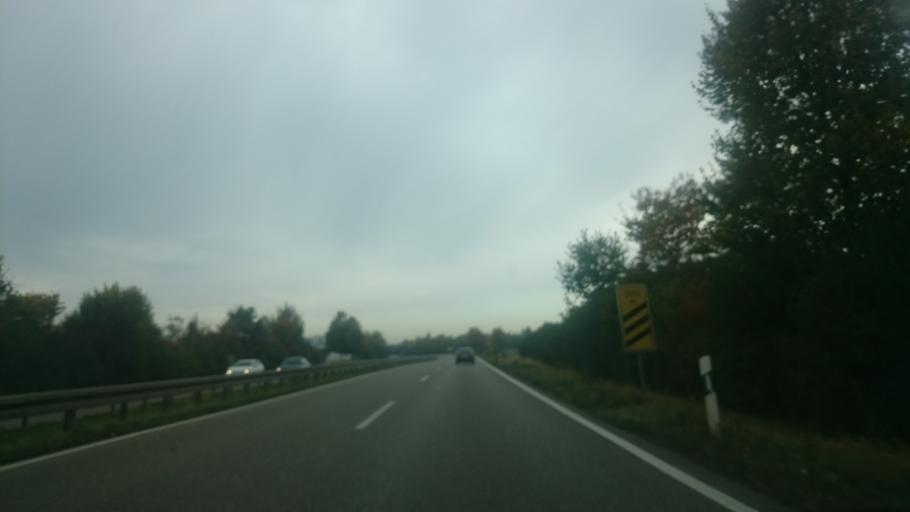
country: DE
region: Bavaria
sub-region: Swabia
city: Westendorf
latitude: 48.5682
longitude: 10.8474
